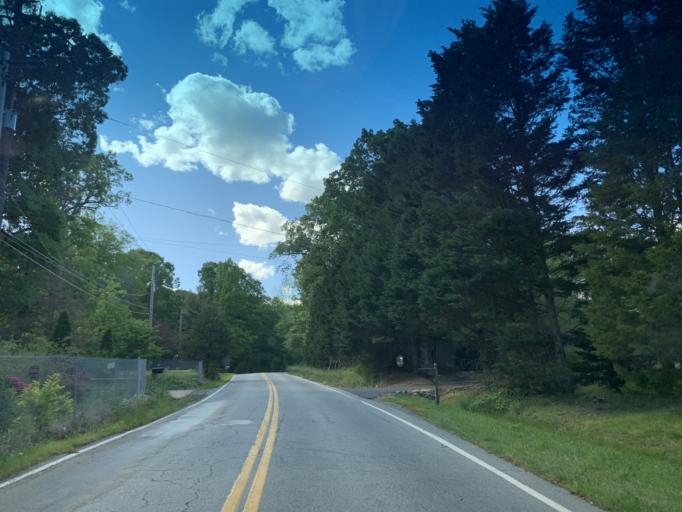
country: US
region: Maryland
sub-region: Cecil County
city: North East
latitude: 39.5750
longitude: -75.9412
